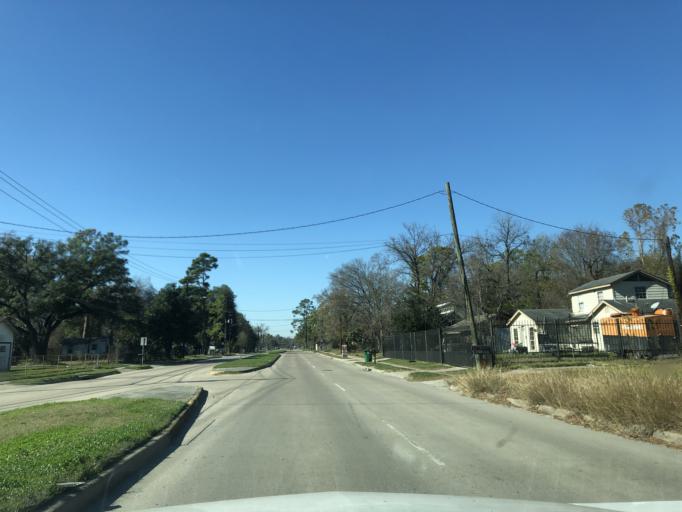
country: US
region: Texas
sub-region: Harris County
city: Jacinto City
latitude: 29.8314
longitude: -95.2946
